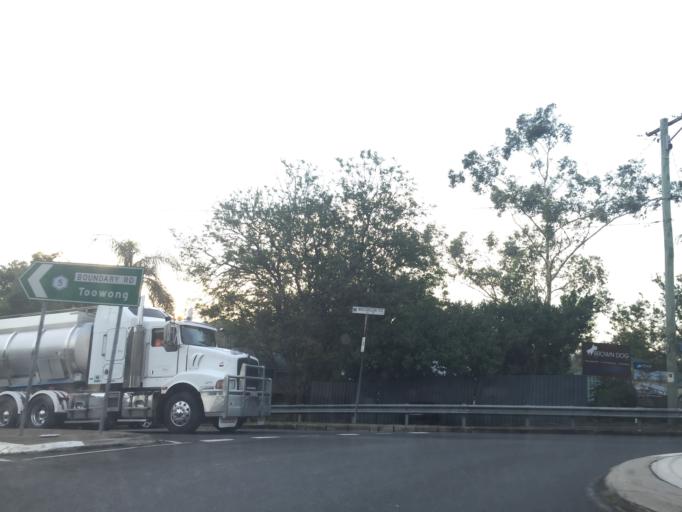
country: AU
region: Queensland
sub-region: Brisbane
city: Milton
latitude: -27.4597
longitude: 152.9887
